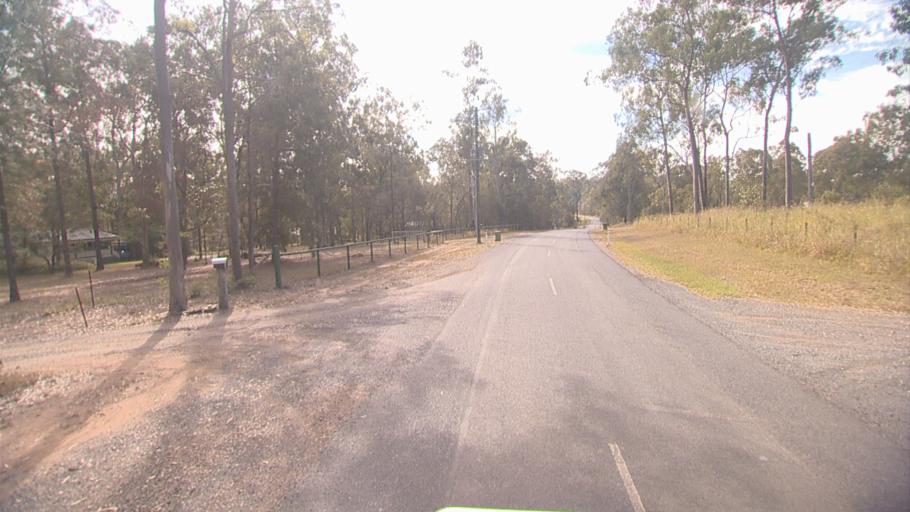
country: AU
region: Queensland
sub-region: Logan
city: North Maclean
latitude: -27.7593
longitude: 152.9714
